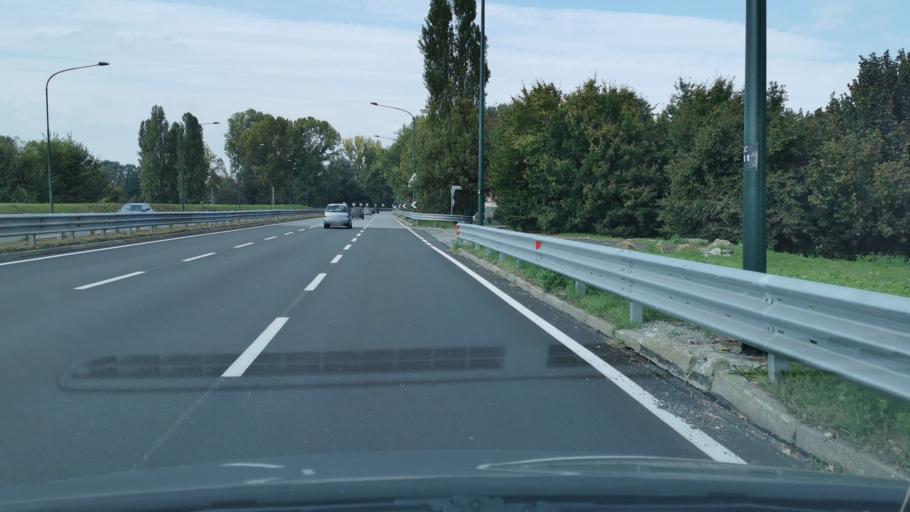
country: IT
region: Piedmont
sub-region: Provincia di Torino
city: San Mauro Torinese
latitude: 45.0865
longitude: 7.7283
